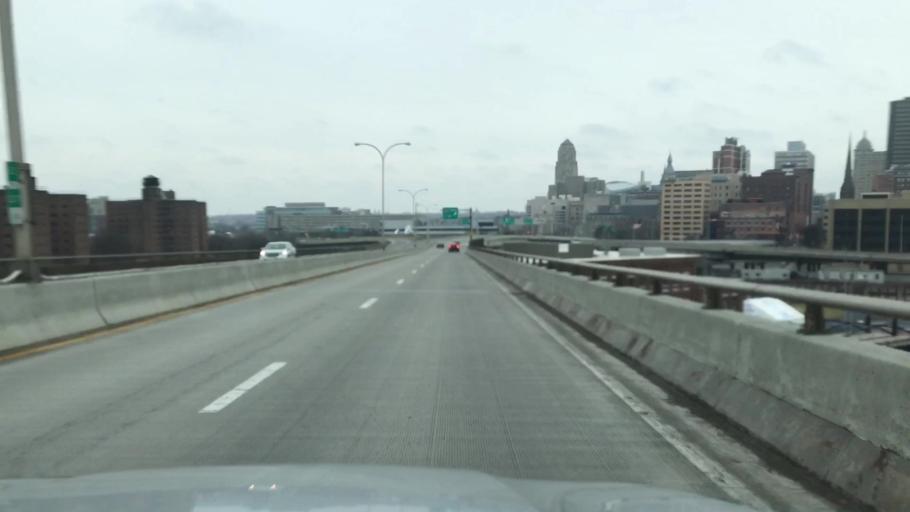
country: US
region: New York
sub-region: Erie County
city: Buffalo
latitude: 42.8768
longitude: -78.8782
